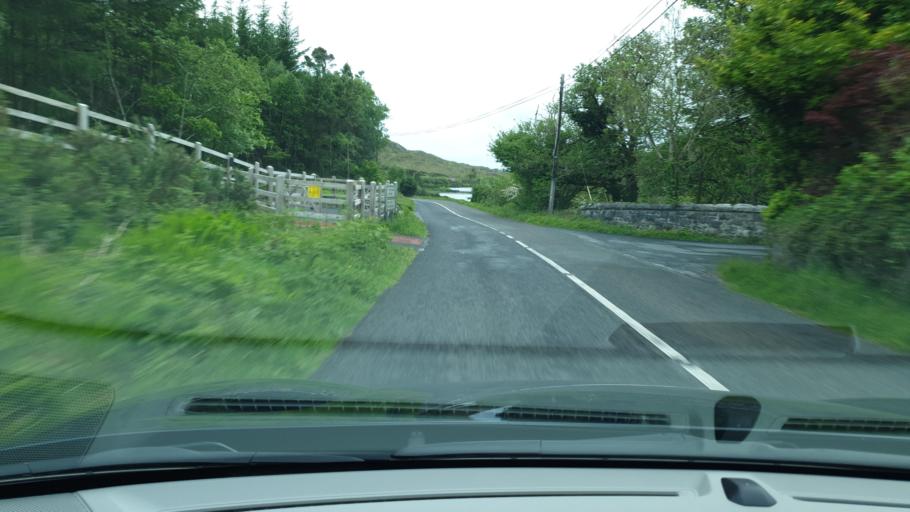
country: IE
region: Connaught
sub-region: County Galway
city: Clifden
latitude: 53.4547
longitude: -9.8673
